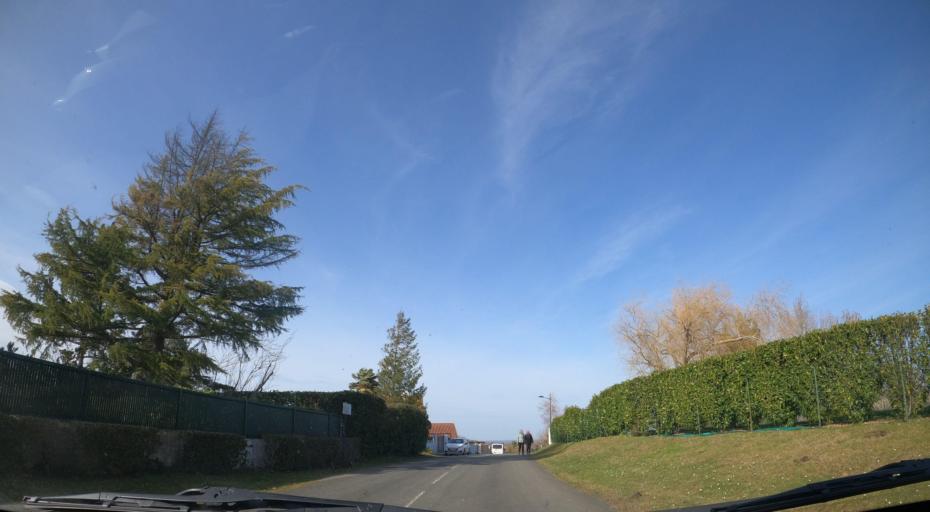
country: FR
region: Aquitaine
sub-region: Departement des Pyrenees-Atlantiques
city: Briscous
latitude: 43.4278
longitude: -1.3752
